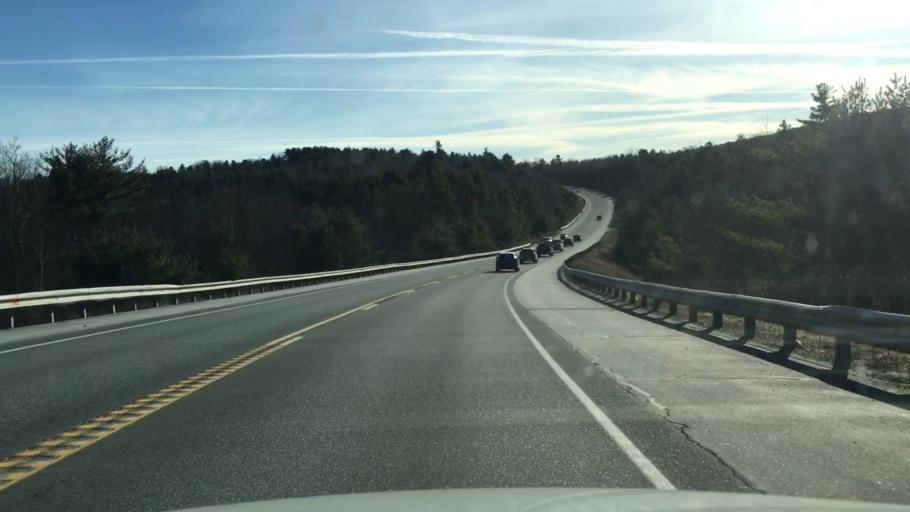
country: US
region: Maine
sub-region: Hancock County
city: Dedham
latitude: 44.6806
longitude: -68.5781
